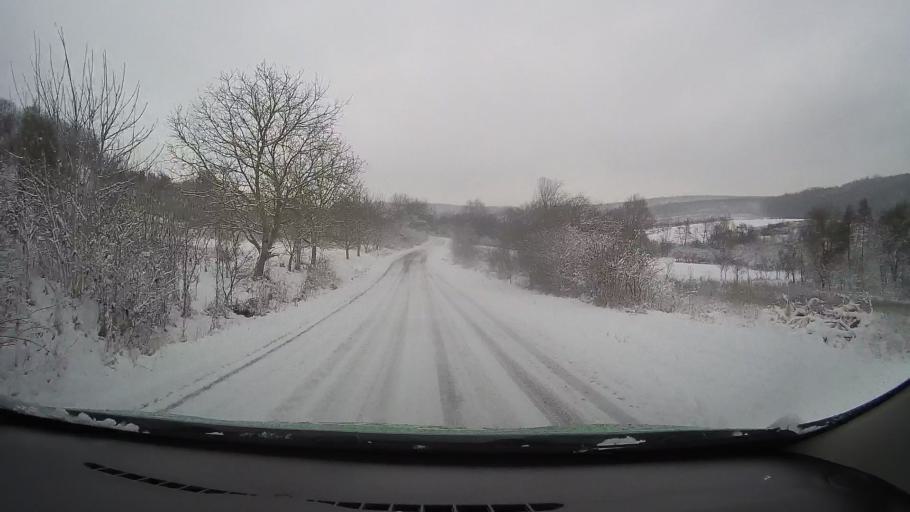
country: RO
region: Hunedoara
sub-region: Comuna Pestisu Mic
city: Pestisu Mic
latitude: 45.8183
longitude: 22.8817
